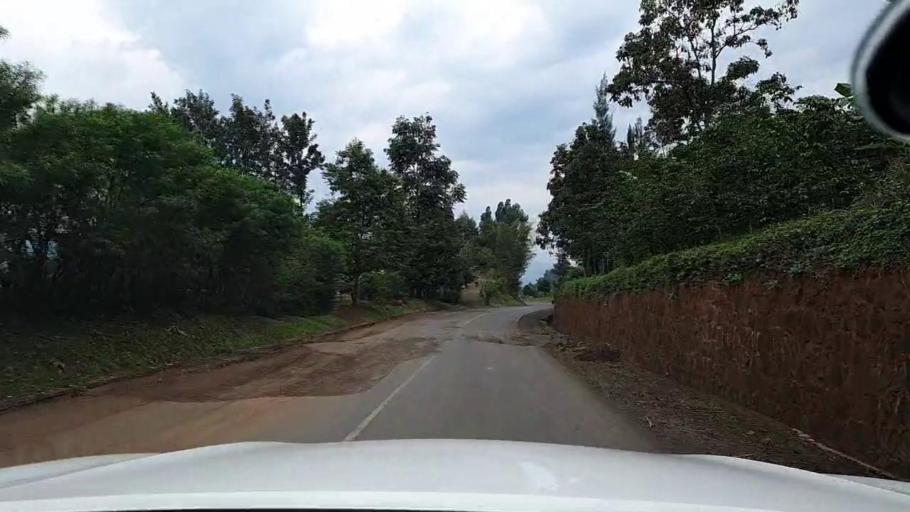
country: RW
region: Western Province
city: Cyangugu
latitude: -2.6579
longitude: 28.9722
